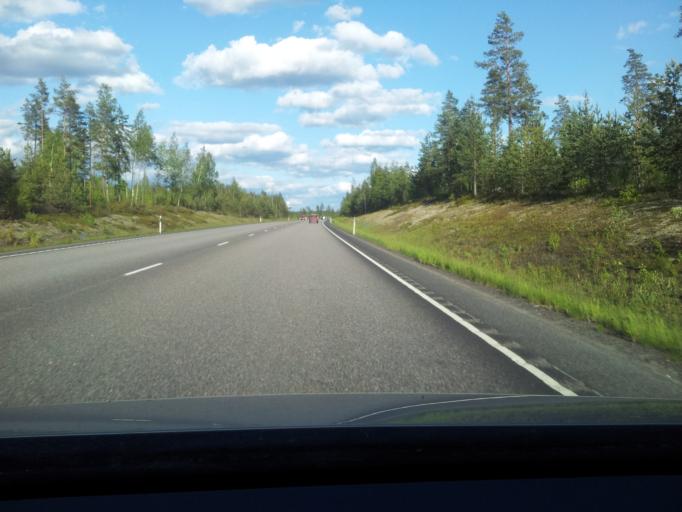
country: FI
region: Kymenlaakso
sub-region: Kouvola
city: Anjala
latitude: 60.9055
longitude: 27.0837
